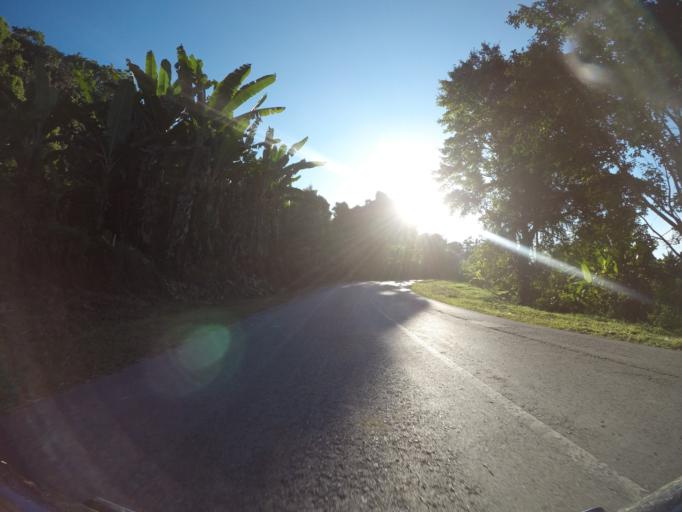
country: TZ
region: Pemba South
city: Mtambile
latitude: -5.3775
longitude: 39.6911
